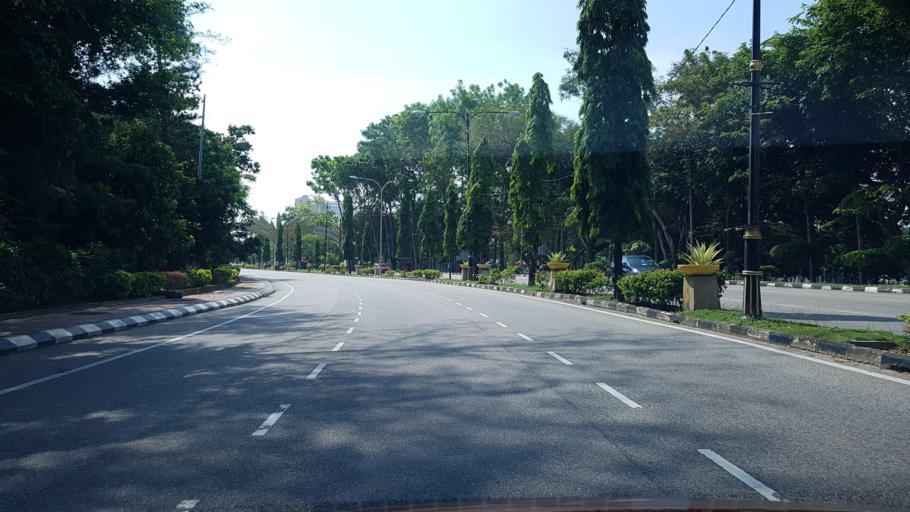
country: MY
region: Terengganu
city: Kuala Terengganu
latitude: 5.3209
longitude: 103.1528
